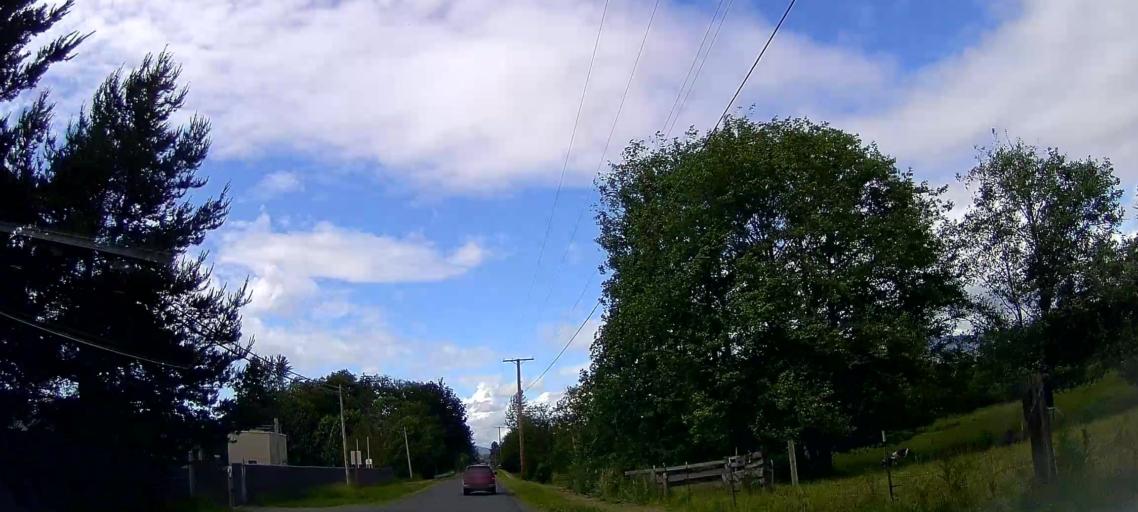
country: US
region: Washington
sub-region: Skagit County
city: Sedro-Woolley
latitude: 48.4932
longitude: -122.2375
